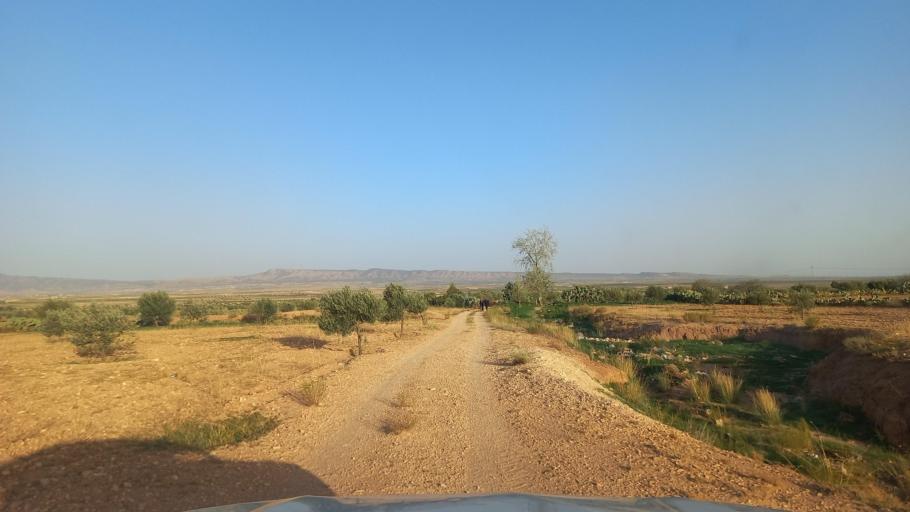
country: TN
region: Al Qasrayn
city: Sbiba
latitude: 35.3707
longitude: 9.0125
